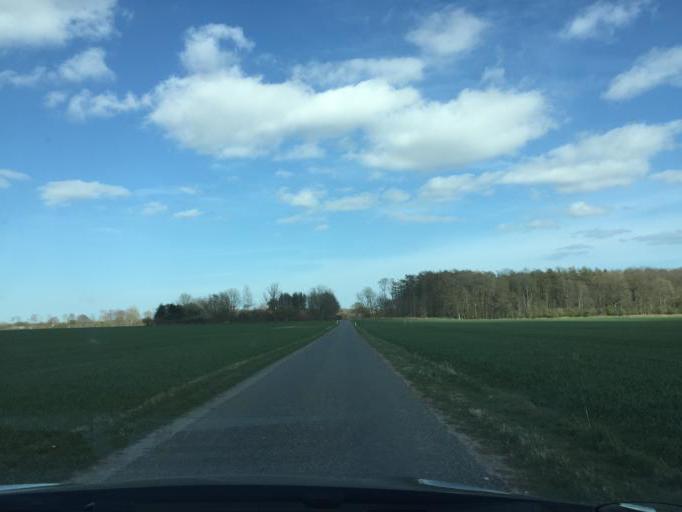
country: DK
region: South Denmark
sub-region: Kerteminde Kommune
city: Langeskov
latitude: 55.3060
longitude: 10.5482
